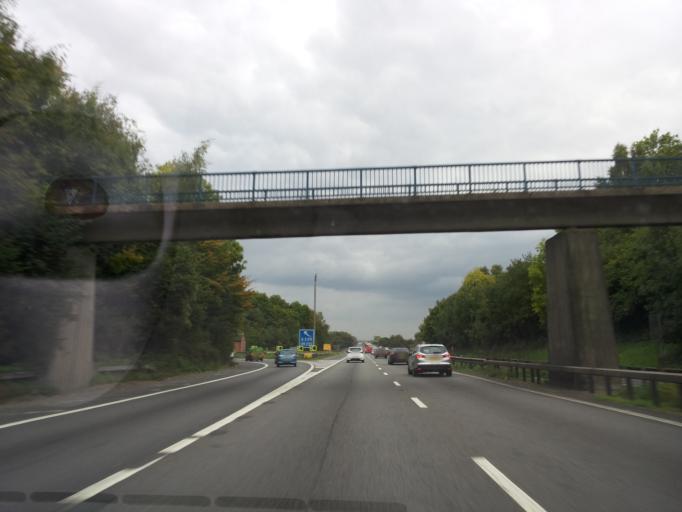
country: GB
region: England
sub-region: Kent
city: Newington
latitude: 51.3317
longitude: 0.6580
